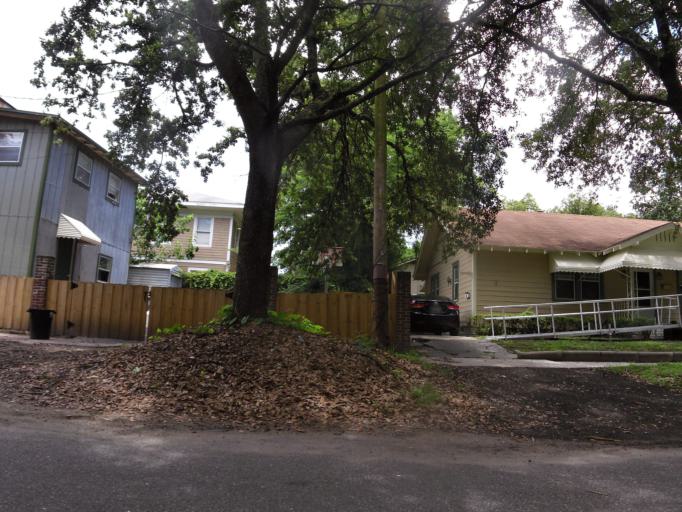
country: US
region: Florida
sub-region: Duval County
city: Jacksonville
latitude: 30.3130
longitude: -81.6984
